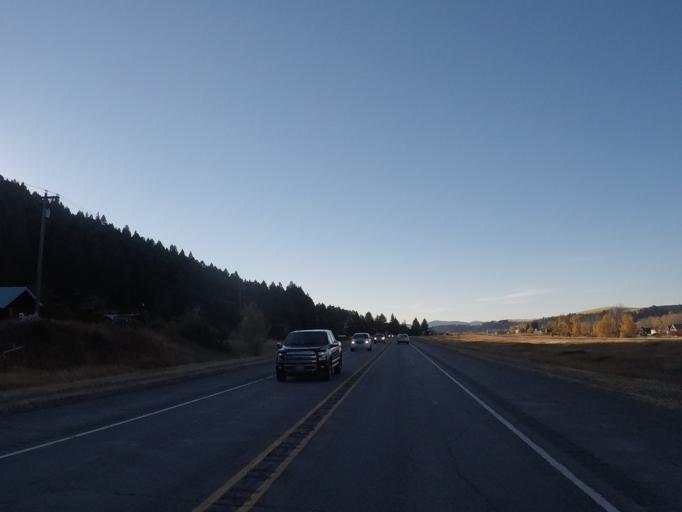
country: US
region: Montana
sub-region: Lewis and Clark County
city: Helena West Side
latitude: 46.5583
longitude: -112.4214
